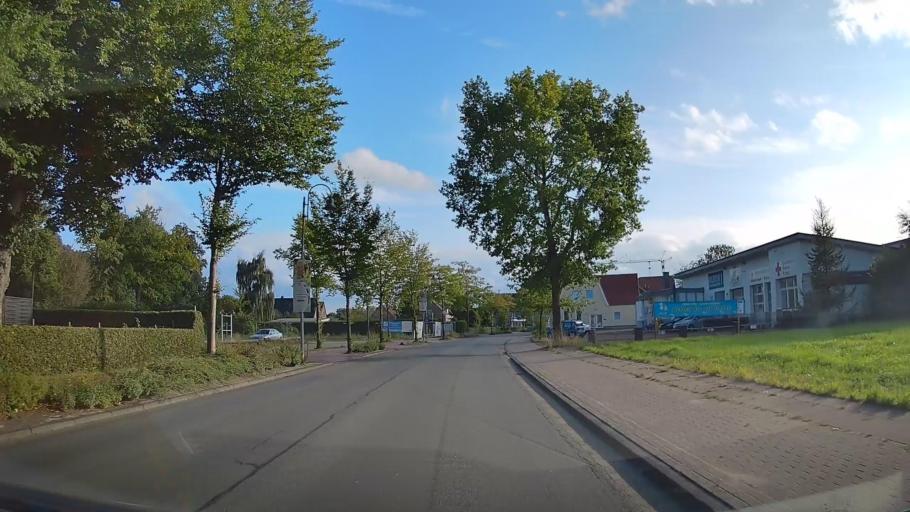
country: DE
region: Lower Saxony
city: Ostrhauderfehn
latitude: 53.1287
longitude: 7.6676
